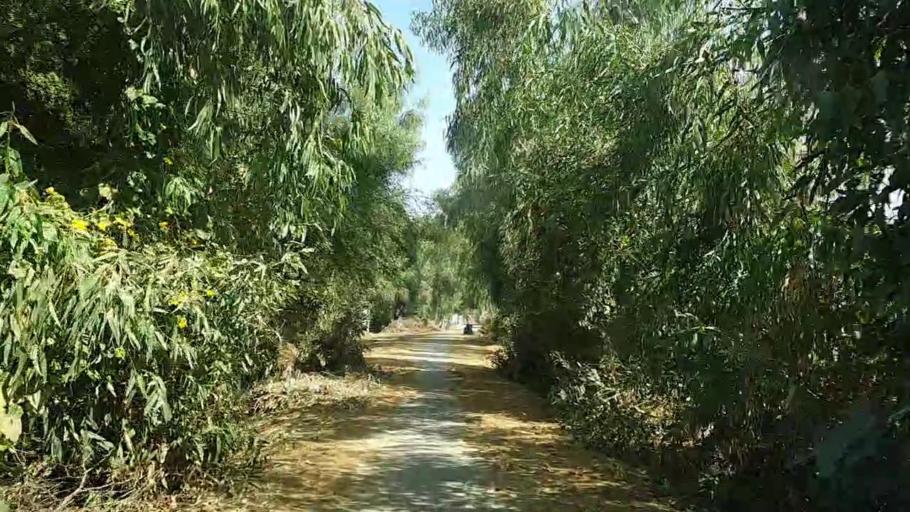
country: PK
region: Sindh
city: Thul
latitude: 28.2576
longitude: 68.8253
